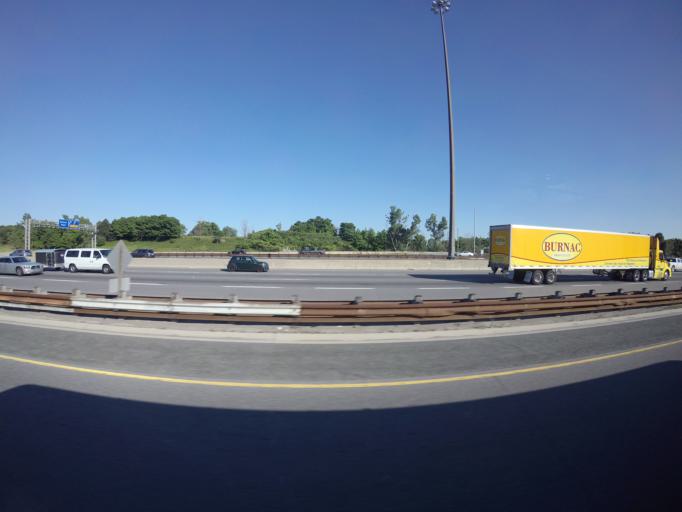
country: CA
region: Ontario
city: Scarborough
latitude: 43.7900
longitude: -79.2246
